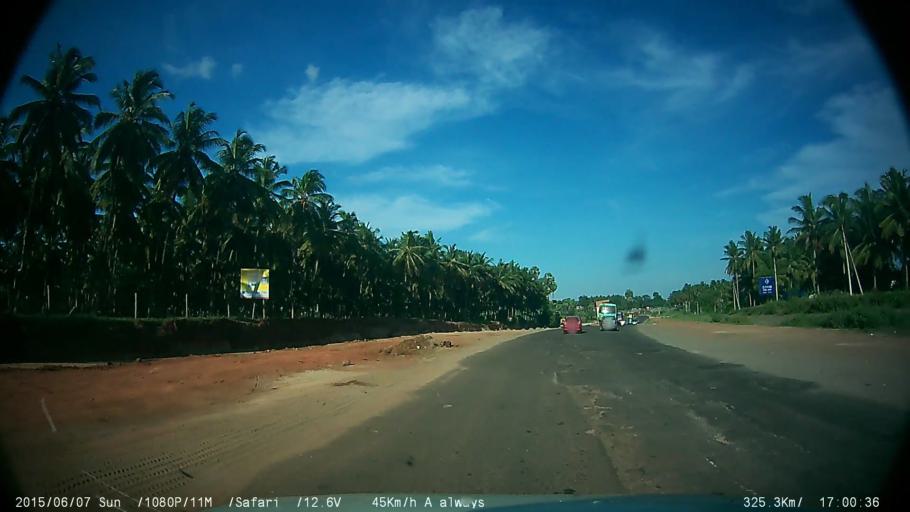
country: IN
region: Tamil Nadu
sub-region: Coimbatore
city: Madukkarai
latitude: 10.8549
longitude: 76.8502
